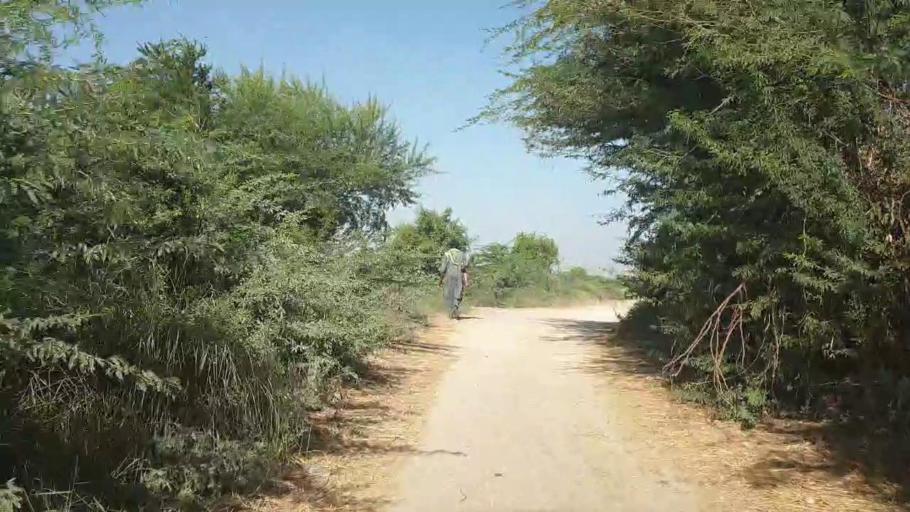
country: PK
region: Sindh
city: Talhar
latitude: 24.7920
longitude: 68.7967
